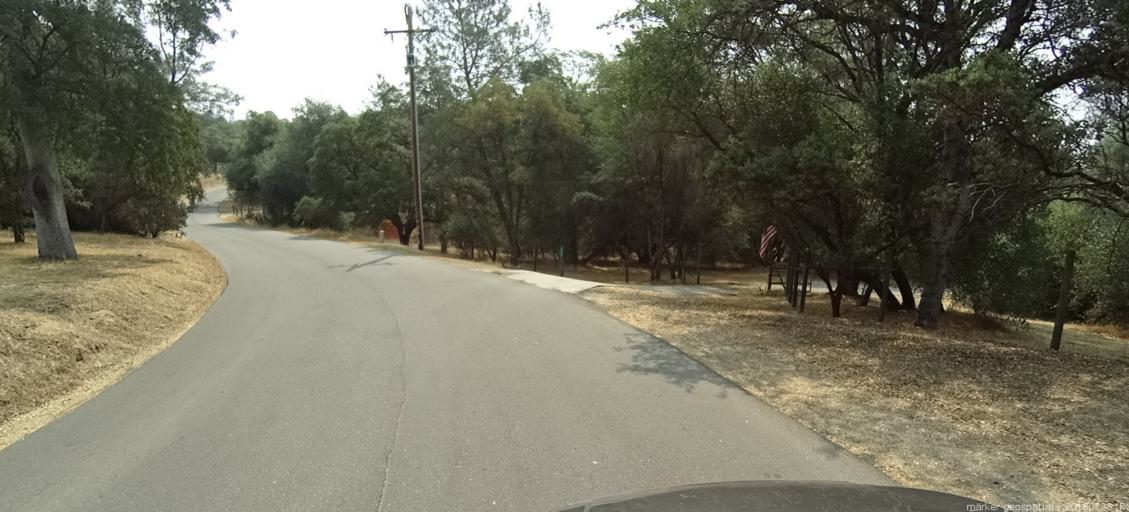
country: US
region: California
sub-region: Madera County
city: Coarsegold
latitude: 37.2337
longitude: -119.7033
